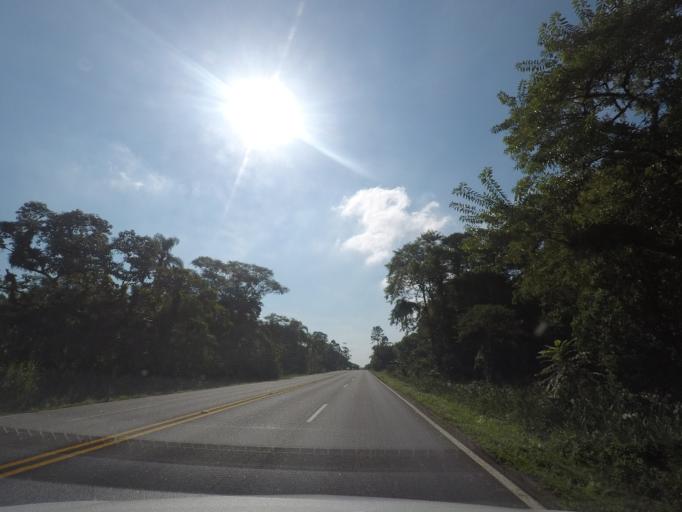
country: BR
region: Parana
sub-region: Pontal Do Parana
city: Pontal do Parana
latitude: -25.6406
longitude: -48.5916
